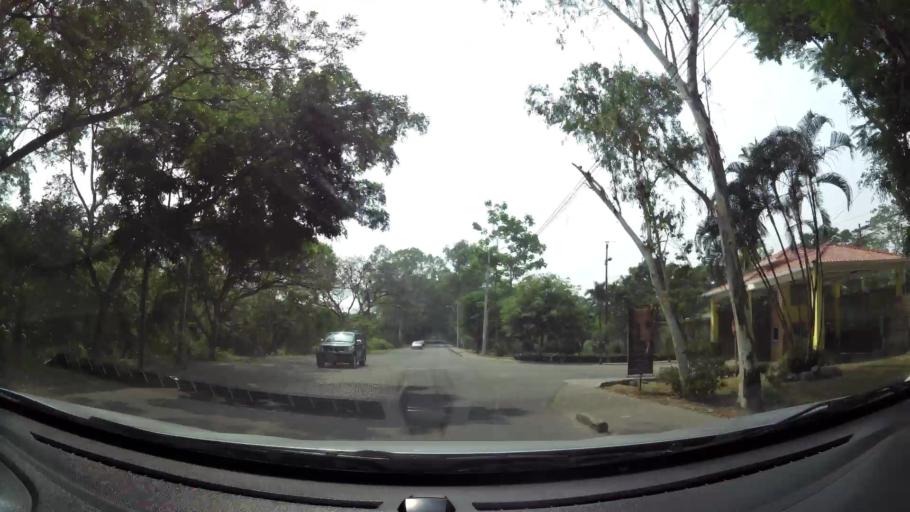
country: HN
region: Cortes
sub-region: San Pedro Sula
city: Pena Blanca
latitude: 15.5658
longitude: -88.0269
